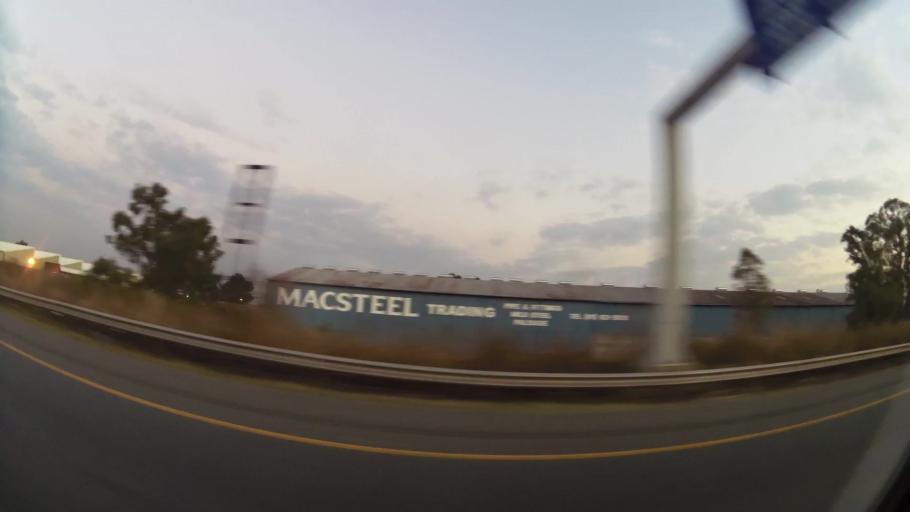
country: ZA
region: Gauteng
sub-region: Ekurhuleni Metropolitan Municipality
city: Germiston
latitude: -26.2574
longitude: 28.1807
